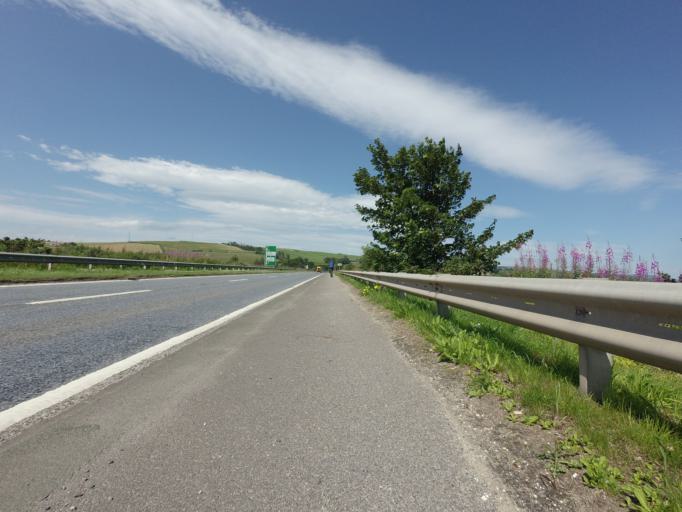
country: GB
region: Scotland
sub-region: Highland
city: Conon Bridge
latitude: 57.5757
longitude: -4.4326
